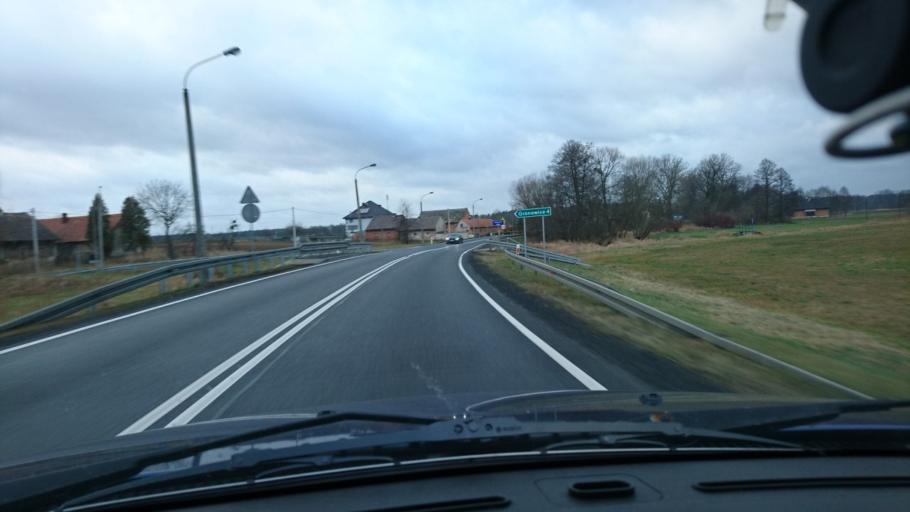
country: PL
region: Opole Voivodeship
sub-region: Powiat oleski
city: Olesno
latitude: 50.9125
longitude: 18.3508
